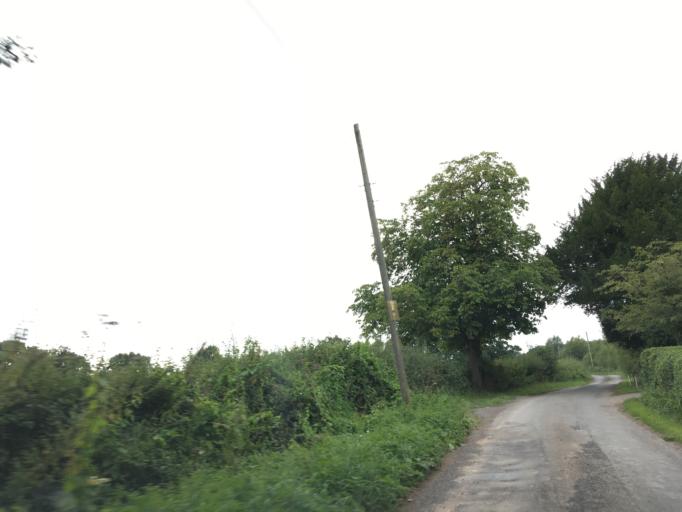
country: GB
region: England
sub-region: South Gloucestershire
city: Falfield
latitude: 51.6475
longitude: -2.4706
